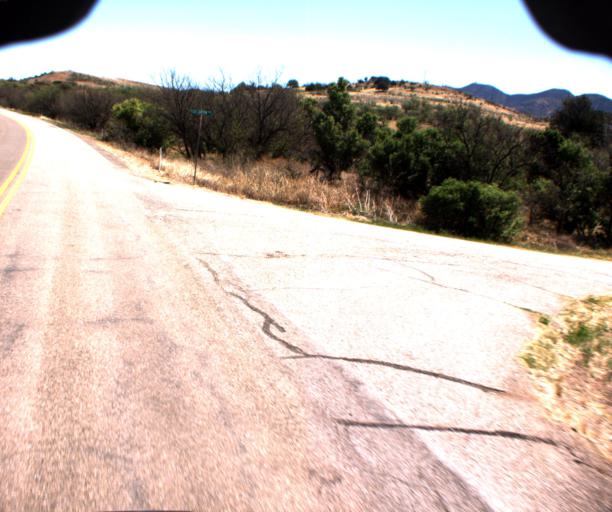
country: US
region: Arizona
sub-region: Santa Cruz County
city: Rio Rico
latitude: 31.5159
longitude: -110.7849
